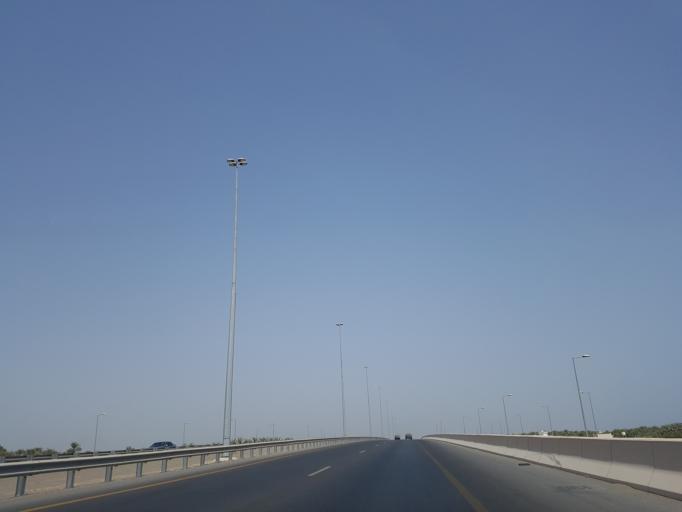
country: OM
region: Al Batinah
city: Saham
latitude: 24.0731
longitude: 56.9480
